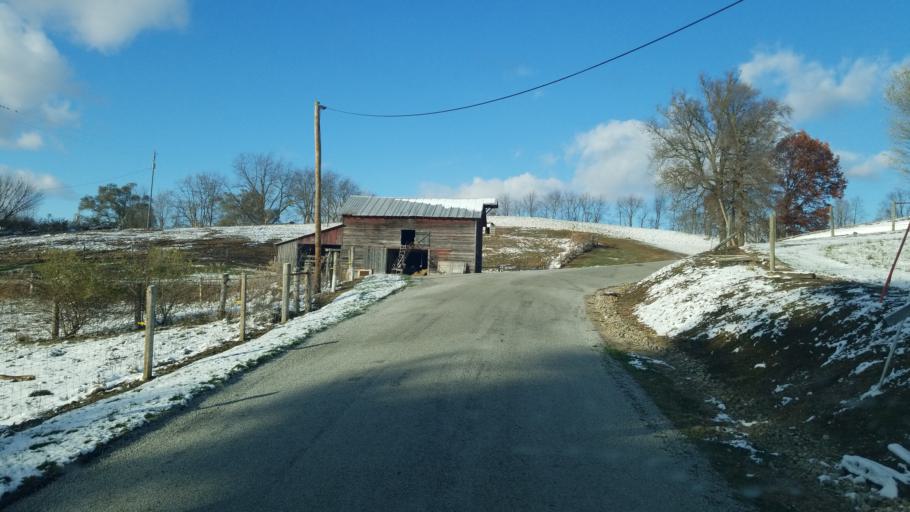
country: US
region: Ohio
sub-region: Licking County
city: Newark
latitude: 40.1444
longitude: -82.3877
